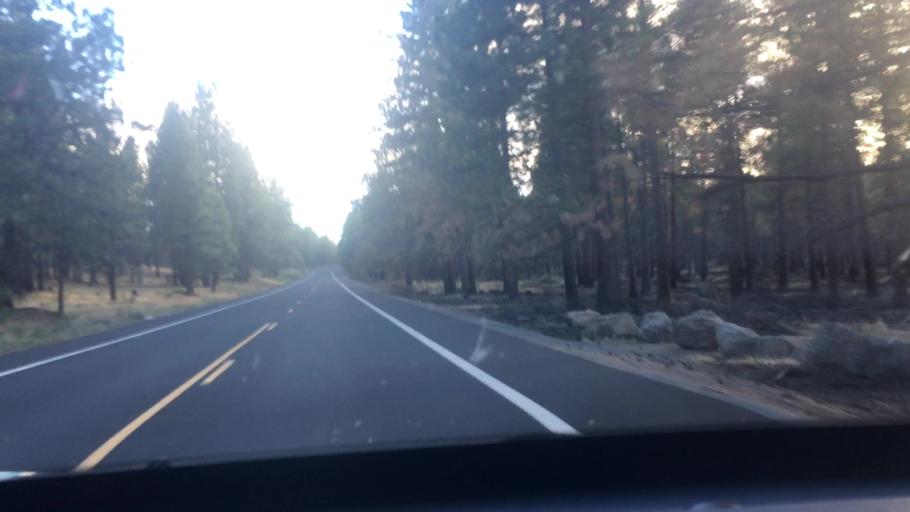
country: US
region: Oregon
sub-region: Deschutes County
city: Deschutes River Woods
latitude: 44.0479
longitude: -121.3941
